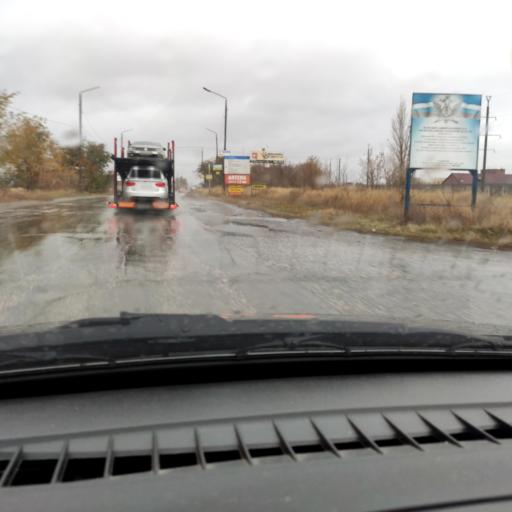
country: RU
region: Samara
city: Tol'yatti
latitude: 53.5729
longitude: 49.3410
